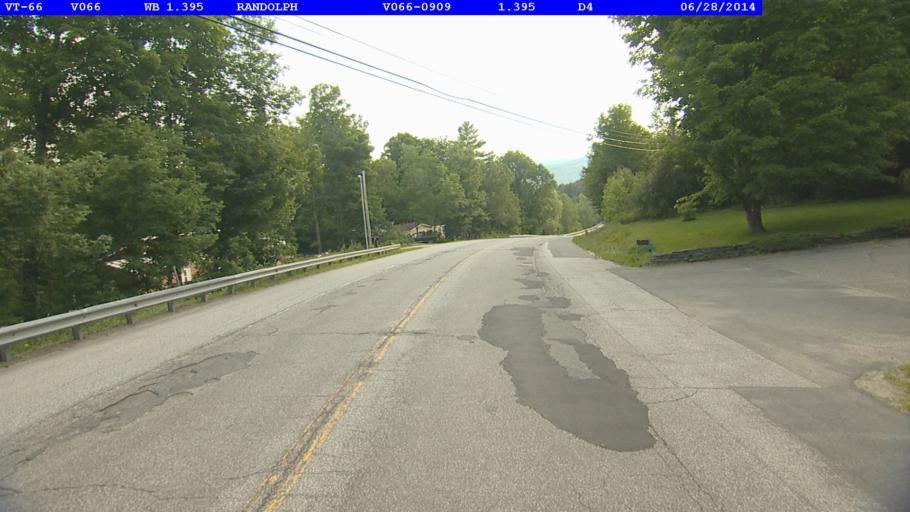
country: US
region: Vermont
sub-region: Orange County
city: Randolph
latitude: 43.9357
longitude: -72.6402
